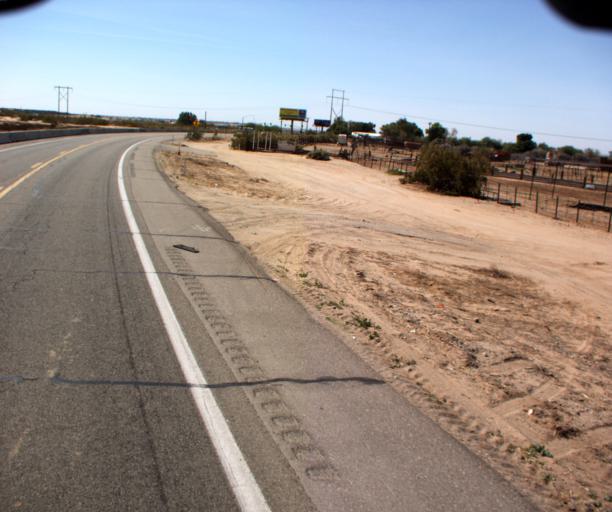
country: US
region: Arizona
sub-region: Yuma County
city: Fortuna Foothills
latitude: 32.7003
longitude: -114.4417
